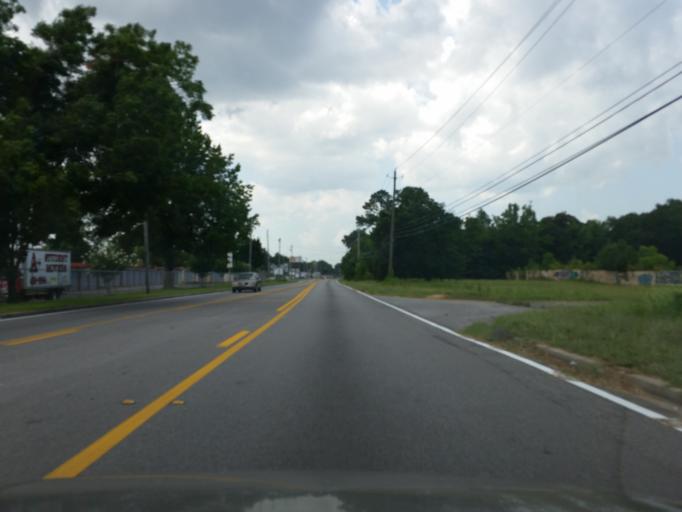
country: US
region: Florida
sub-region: Escambia County
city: Brent
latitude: 30.4783
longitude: -87.2465
